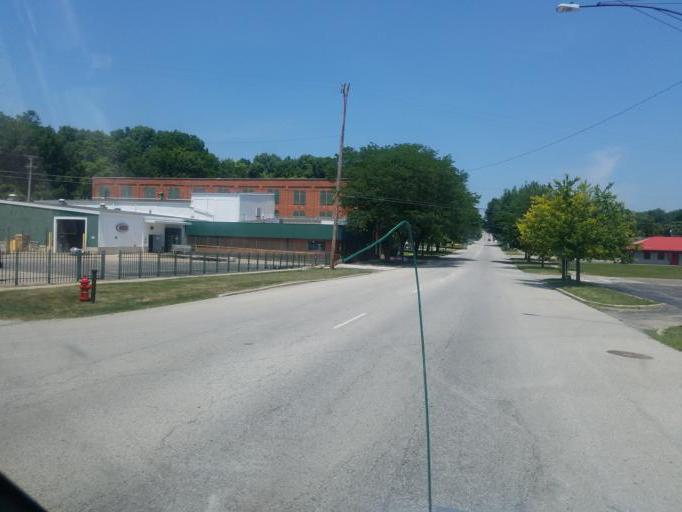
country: US
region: Ohio
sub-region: Shelby County
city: Sidney
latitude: 40.2887
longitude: -84.1550
